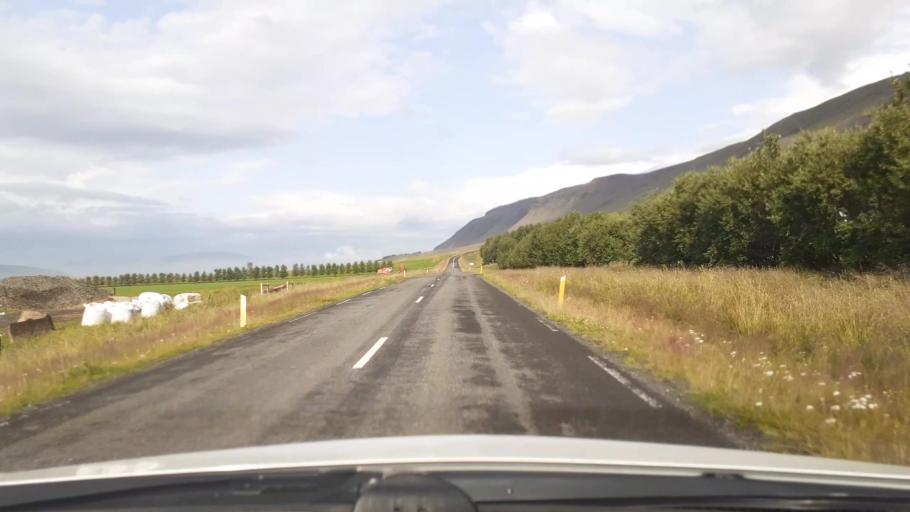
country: IS
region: Capital Region
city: Mosfellsbaer
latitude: 64.3398
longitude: -21.5456
